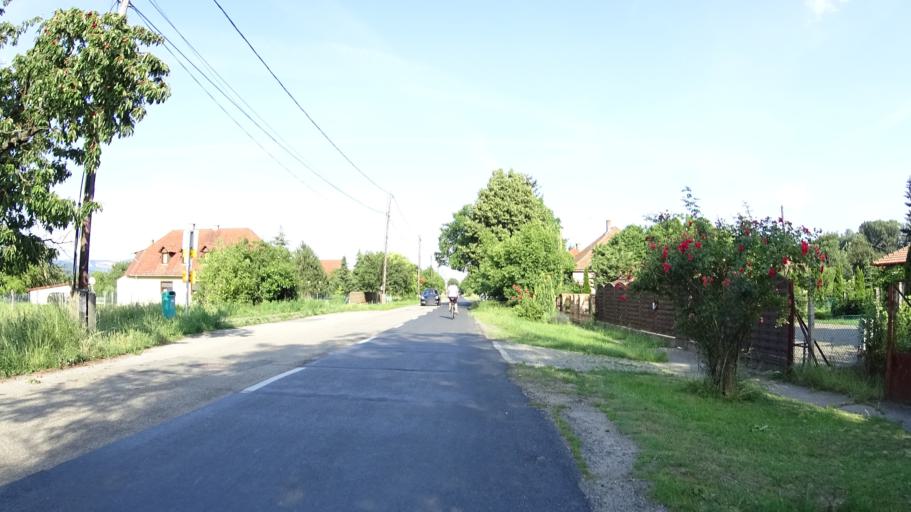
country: HU
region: Pest
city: Veroce
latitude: 47.8055
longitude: 19.0180
